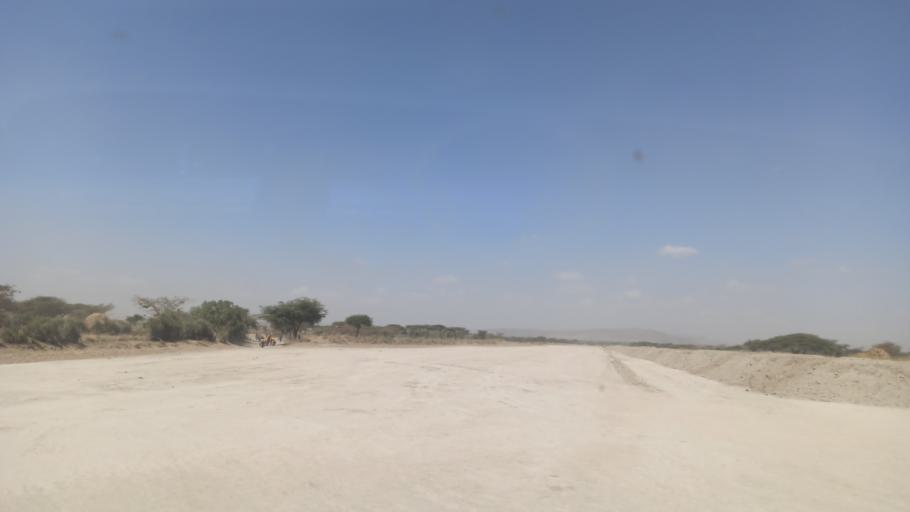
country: ET
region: Oromiya
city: Ziway
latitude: 7.7408
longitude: 38.6199
